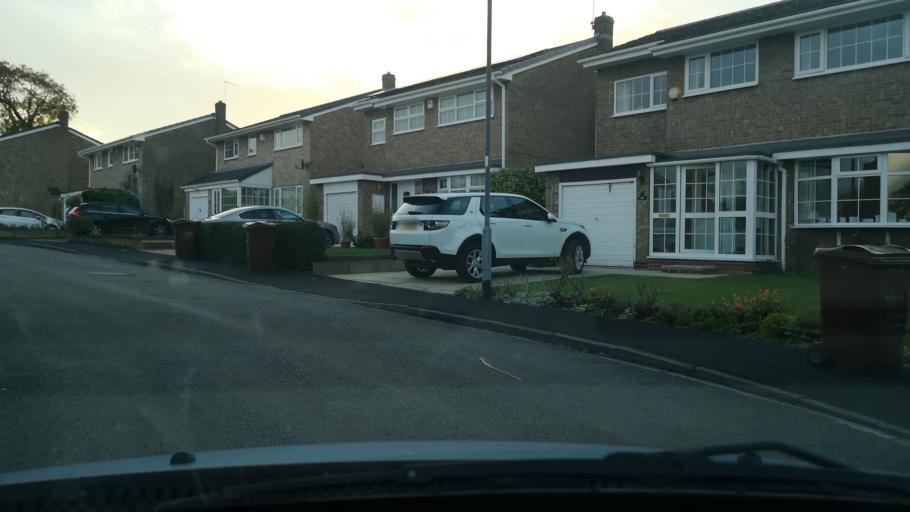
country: GB
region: England
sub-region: City and Borough of Wakefield
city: Low Ackworth
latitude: 53.6461
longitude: -1.3454
